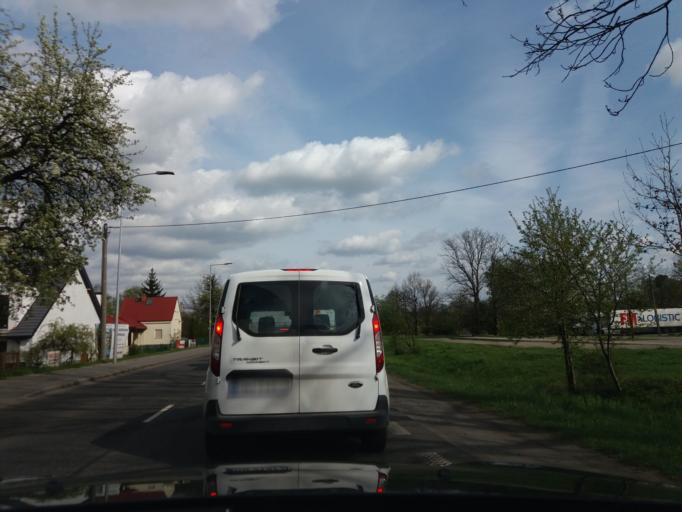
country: PL
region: Lower Silesian Voivodeship
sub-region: Powiat wroclawski
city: Smolec
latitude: 51.1469
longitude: 16.8580
